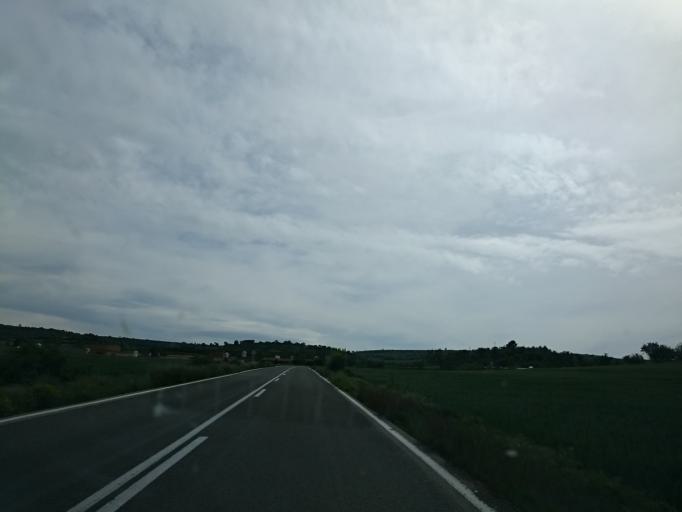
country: ES
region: Catalonia
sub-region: Provincia de Lleida
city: Ivorra
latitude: 41.7768
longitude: 1.3894
